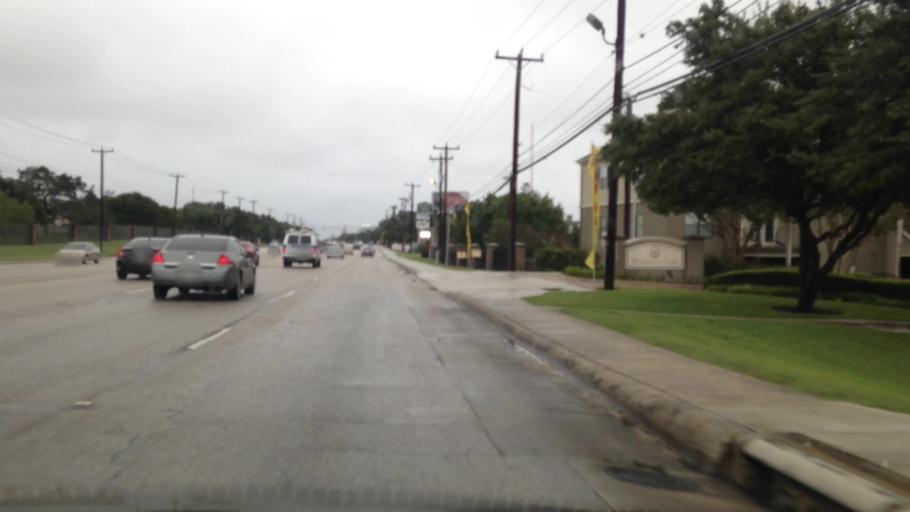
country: US
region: Texas
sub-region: Bexar County
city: Balcones Heights
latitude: 29.5324
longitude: -98.5766
